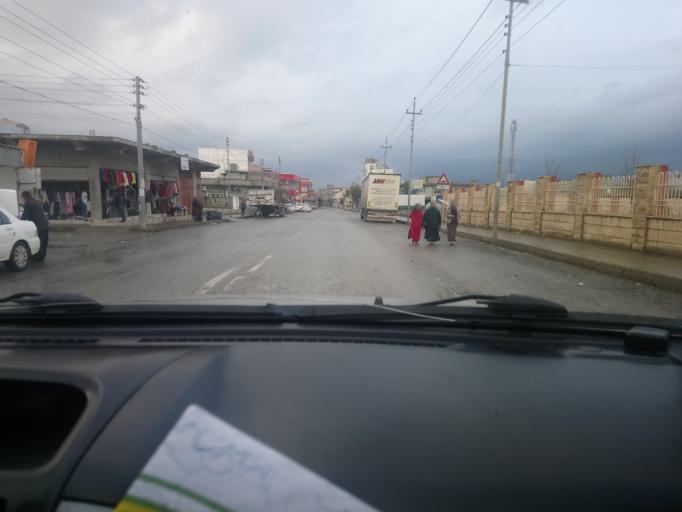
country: IQ
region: As Sulaymaniyah
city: Qeladize
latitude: 36.1819
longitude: 45.1363
